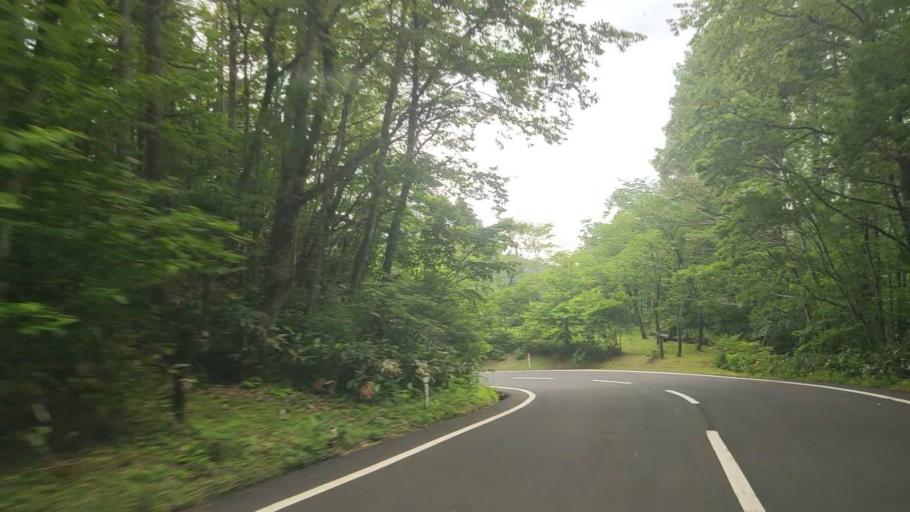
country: JP
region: Tottori
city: Kurayoshi
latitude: 35.3026
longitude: 133.9909
